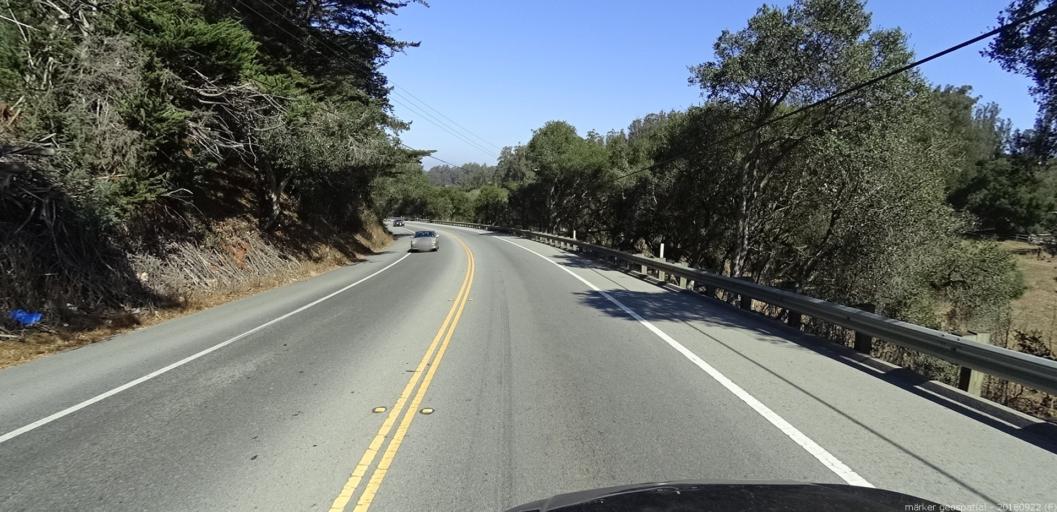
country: US
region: California
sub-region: Monterey County
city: Prunedale
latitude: 36.8334
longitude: -121.6798
